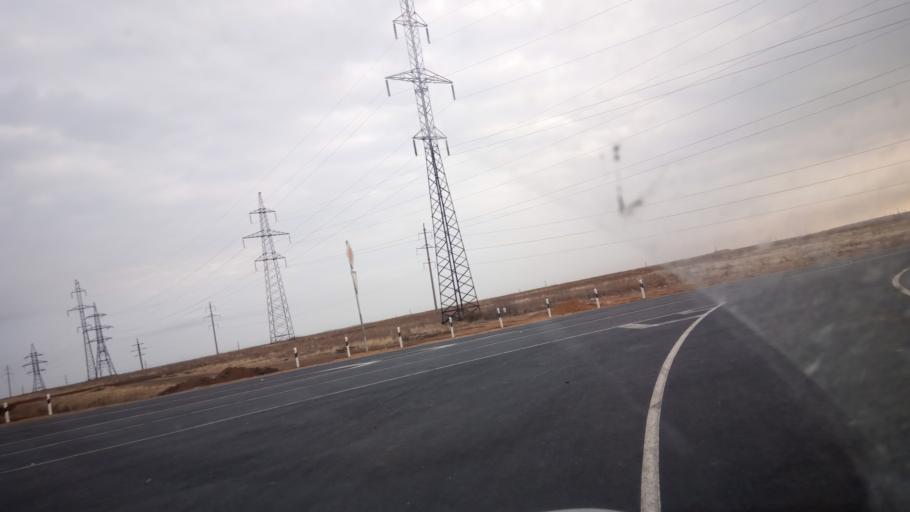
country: RU
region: Orenburg
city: Novotroitsk
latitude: 51.2464
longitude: 58.3189
